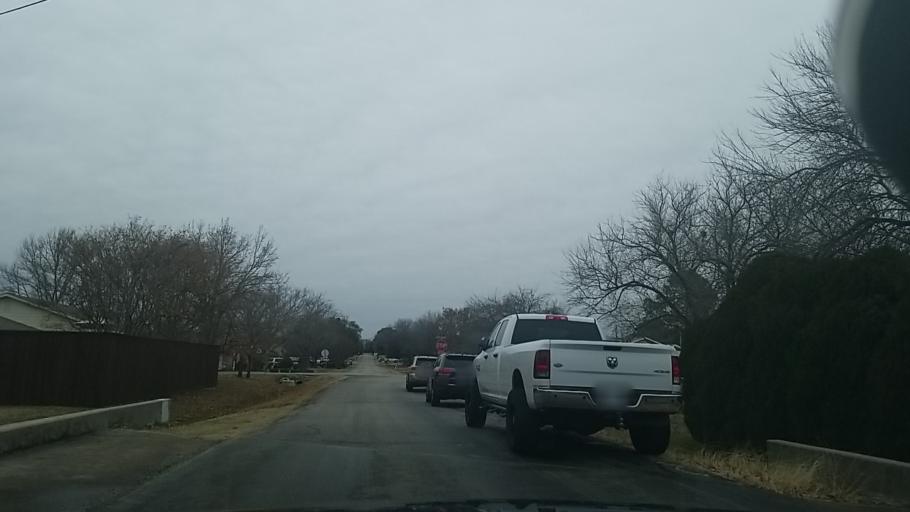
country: US
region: Texas
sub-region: Denton County
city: Corinth
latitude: 33.1484
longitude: -97.0665
